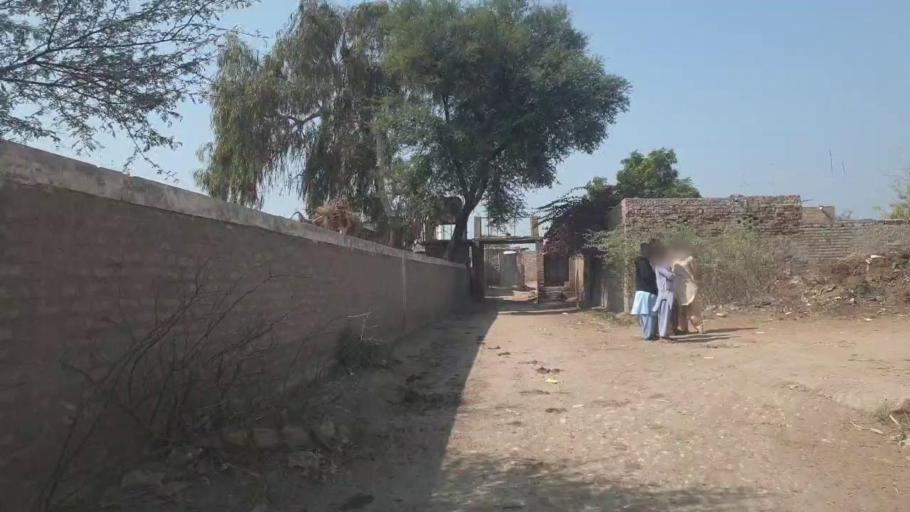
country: PK
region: Sindh
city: Tando Allahyar
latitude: 25.4320
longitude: 68.8360
